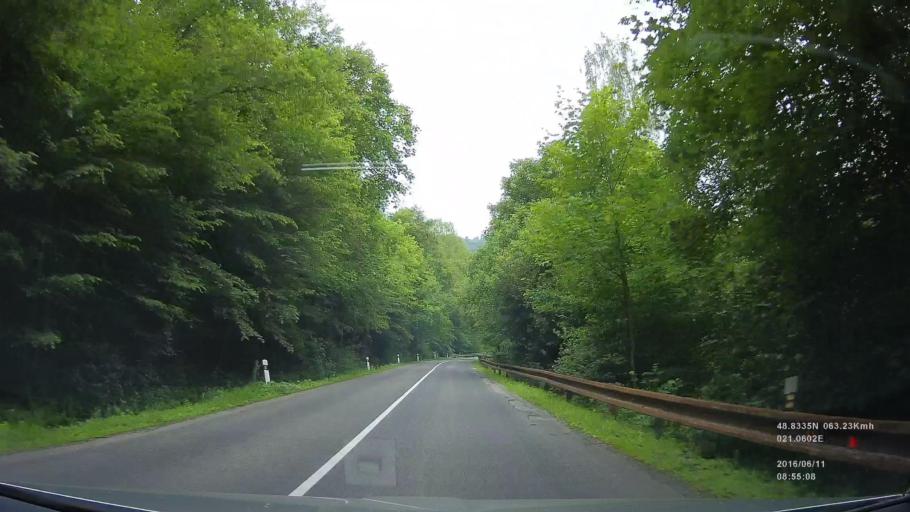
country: SK
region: Kosicky
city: Gelnica
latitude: 48.8104
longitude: 21.0963
